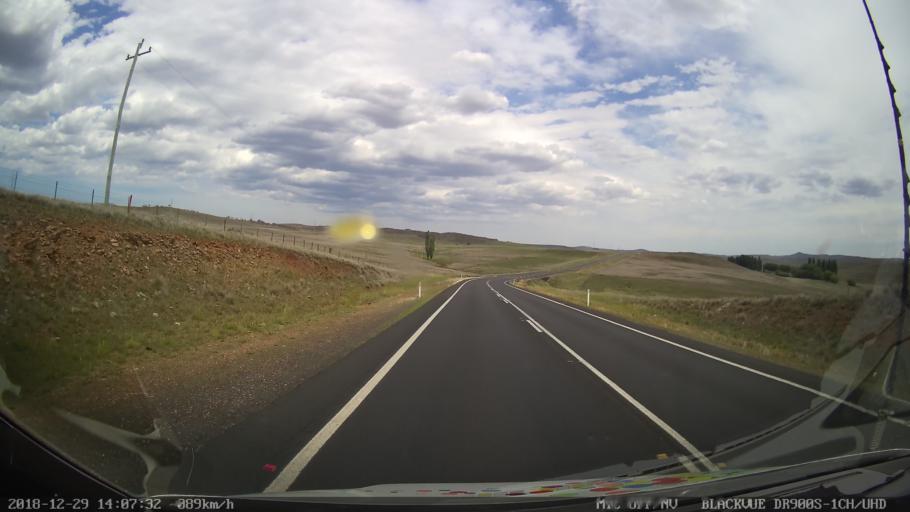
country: AU
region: New South Wales
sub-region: Cooma-Monaro
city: Cooma
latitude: -36.3530
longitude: 149.2143
